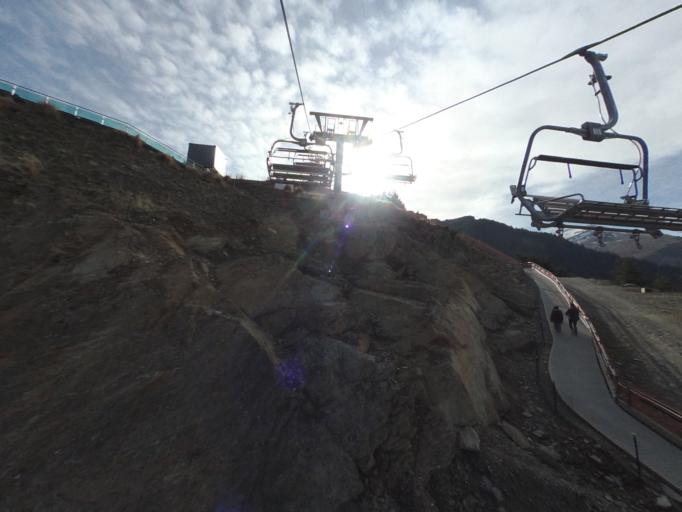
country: NZ
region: Otago
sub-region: Queenstown-Lakes District
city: Queenstown
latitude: -45.0262
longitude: 168.6499
